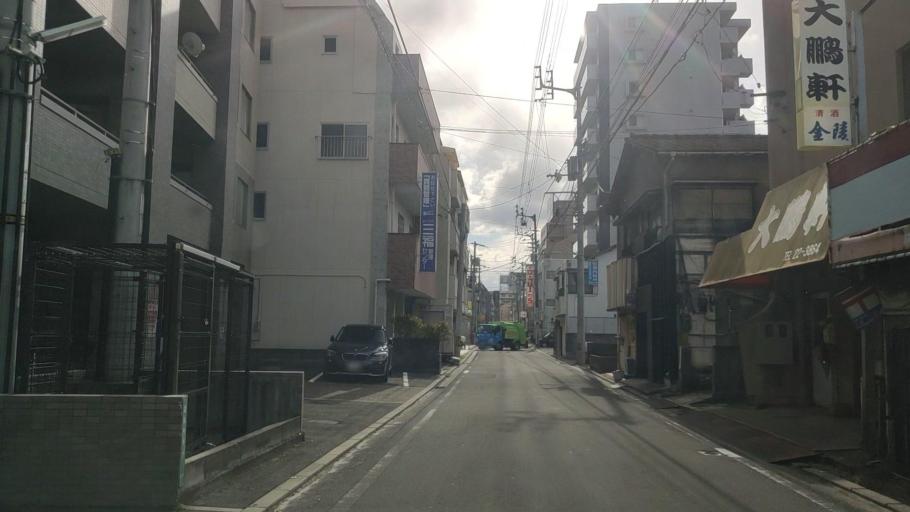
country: JP
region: Ehime
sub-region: Shikoku-chuo Shi
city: Matsuyama
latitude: 33.8509
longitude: 132.7760
